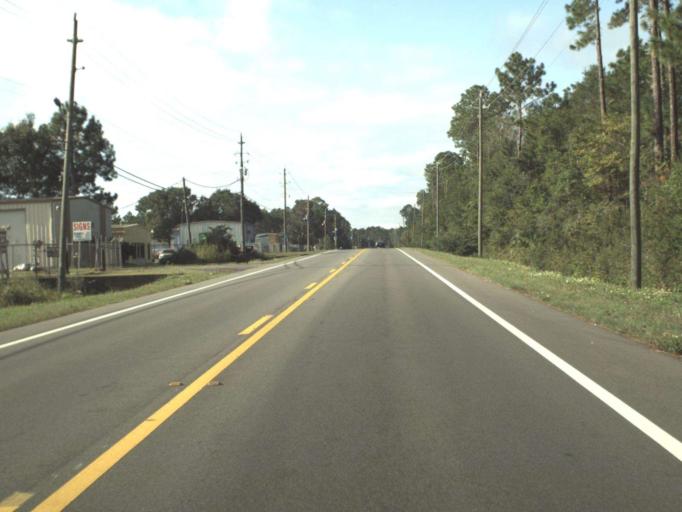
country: US
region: Florida
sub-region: Escambia County
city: Myrtle Grove
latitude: 30.3922
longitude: -87.3114
